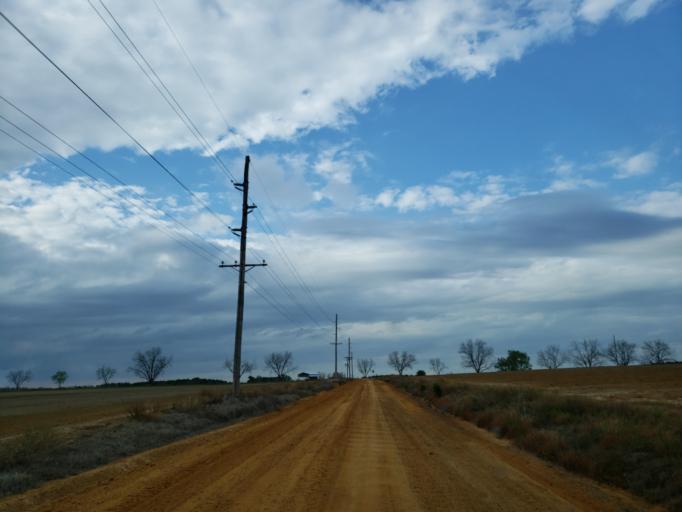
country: US
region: Georgia
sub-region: Dooly County
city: Vienna
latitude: 32.1285
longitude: -83.7040
